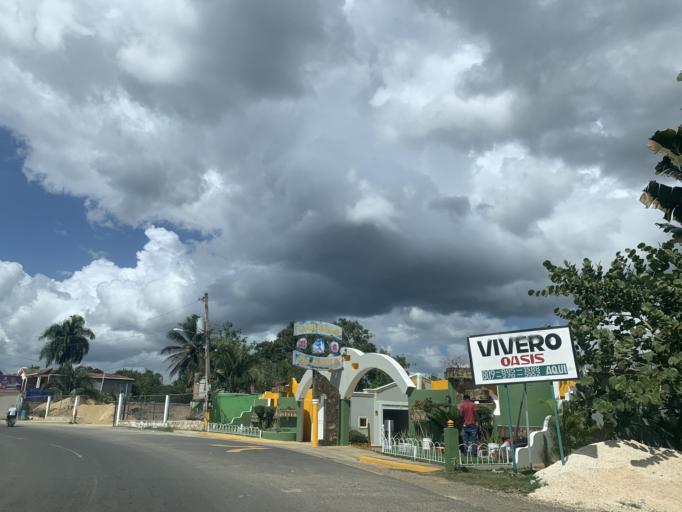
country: DO
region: Monte Plata
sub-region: Yamasa
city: Yamasa
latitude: 18.7642
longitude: -70.0193
